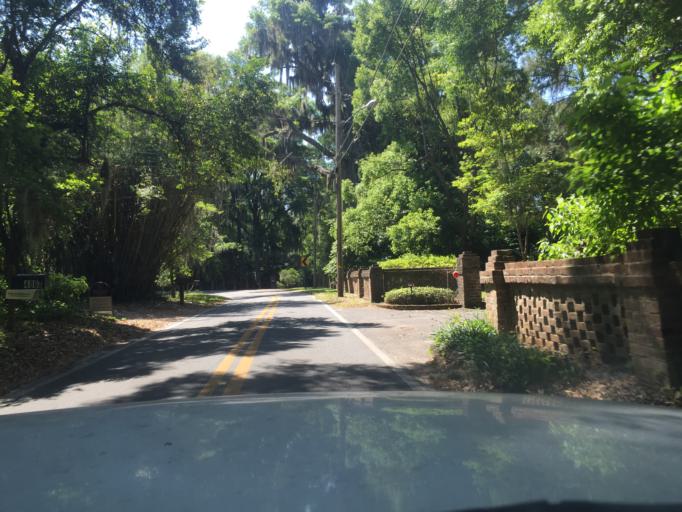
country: US
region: Georgia
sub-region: Chatham County
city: Montgomery
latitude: 31.9353
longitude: -81.1130
